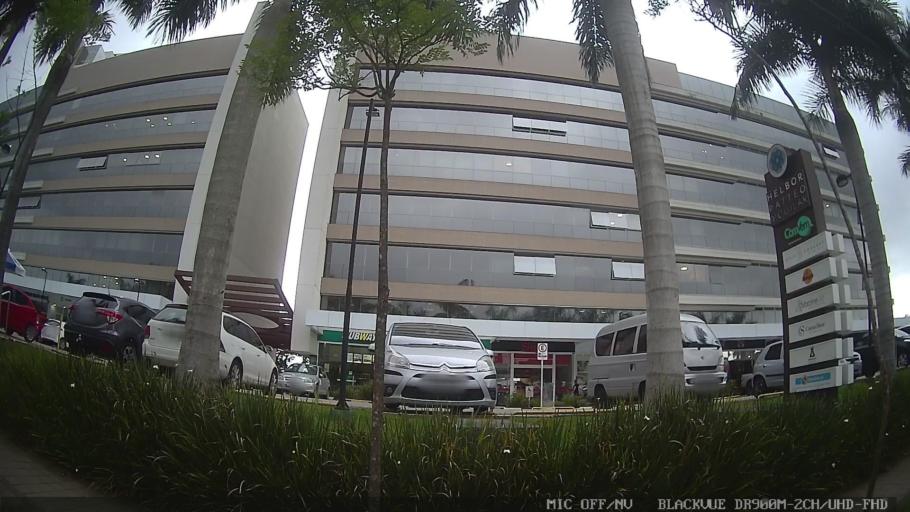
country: BR
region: Sao Paulo
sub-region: Mogi das Cruzes
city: Mogi das Cruzes
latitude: -23.5094
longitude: -46.1930
